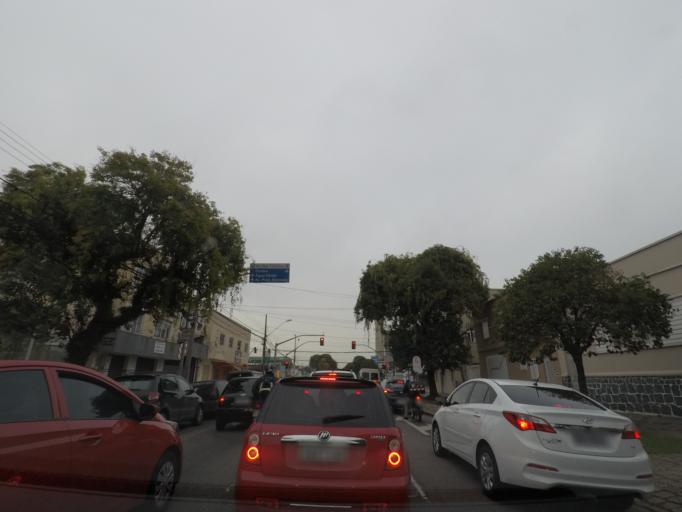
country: BR
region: Parana
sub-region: Curitiba
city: Curitiba
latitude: -25.4494
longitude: -49.2622
